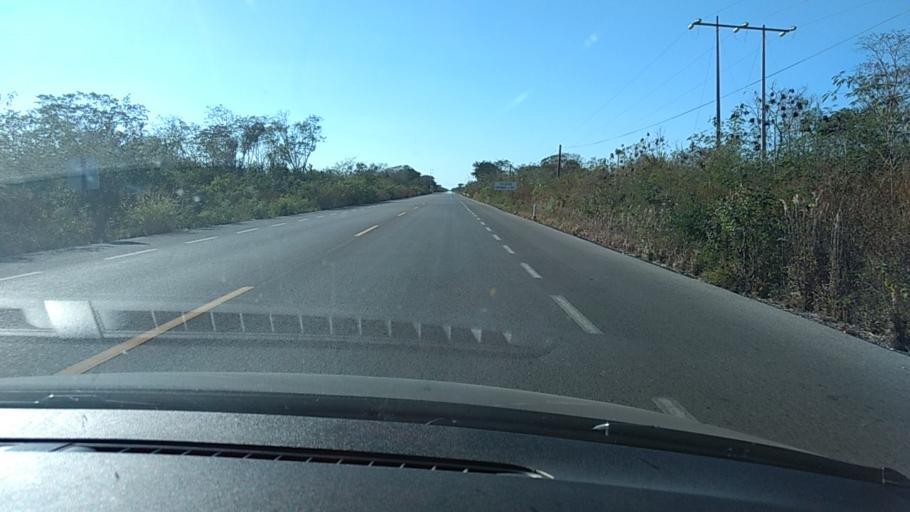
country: MX
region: Yucatan
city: Chichen-Itza
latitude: 20.6308
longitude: -88.4528
